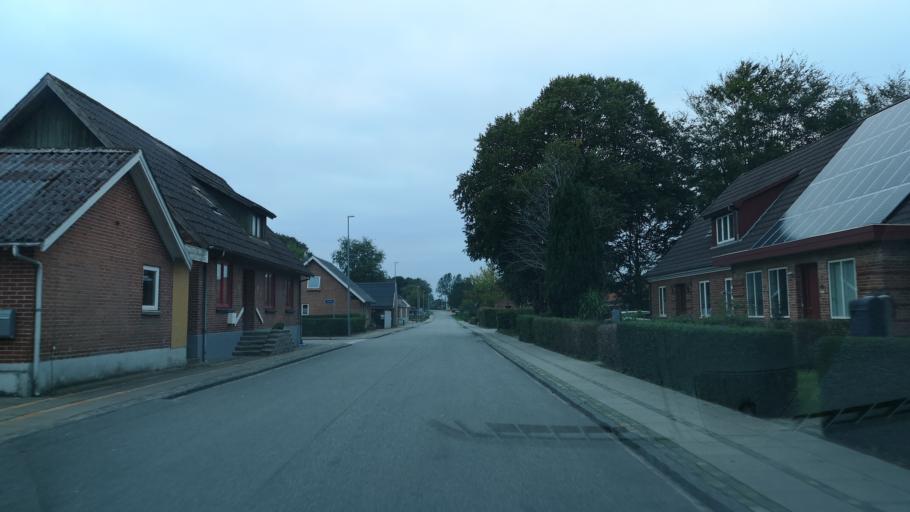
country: DK
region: Central Jutland
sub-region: Ringkobing-Skjern Kommune
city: Videbaek
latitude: 56.0662
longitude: 8.5958
